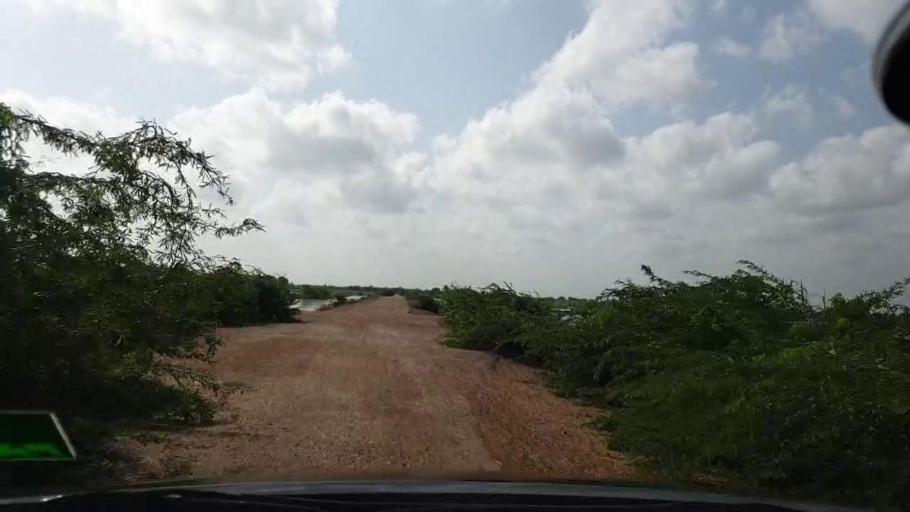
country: PK
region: Sindh
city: Kadhan
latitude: 24.6364
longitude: 69.0884
